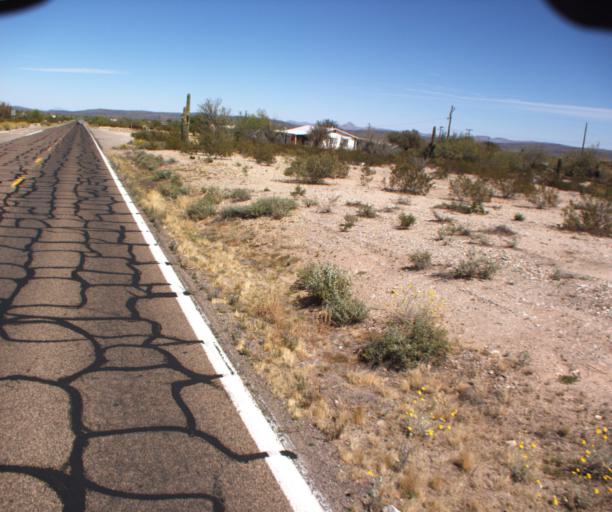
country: US
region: Arizona
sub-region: Pima County
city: Ajo
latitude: 32.4038
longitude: -112.8719
